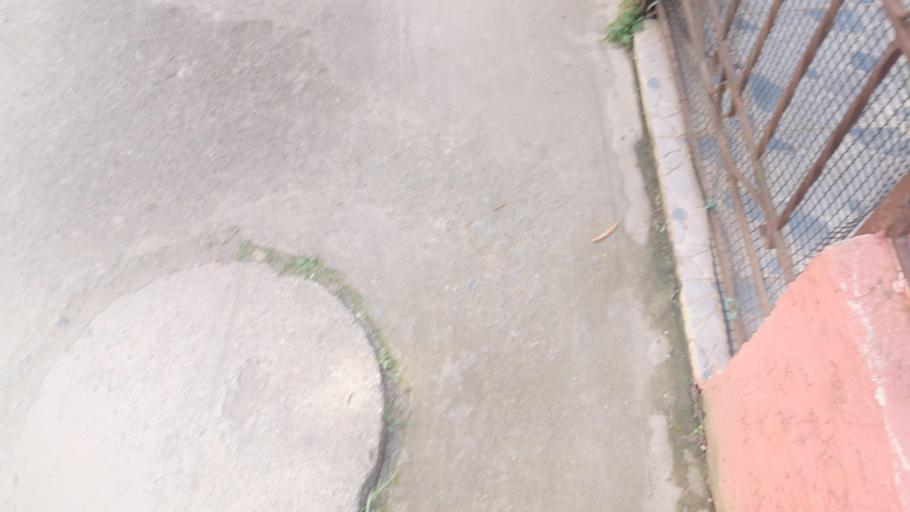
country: CO
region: Valle del Cauca
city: Jamundi
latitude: 3.2558
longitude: -76.5481
